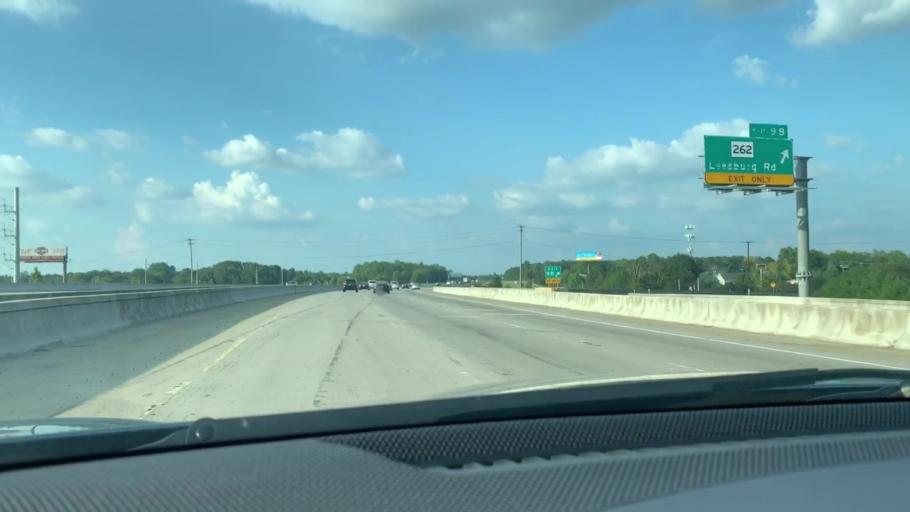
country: US
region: South Carolina
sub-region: Richland County
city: Forest Acres
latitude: 33.9739
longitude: -80.9550
